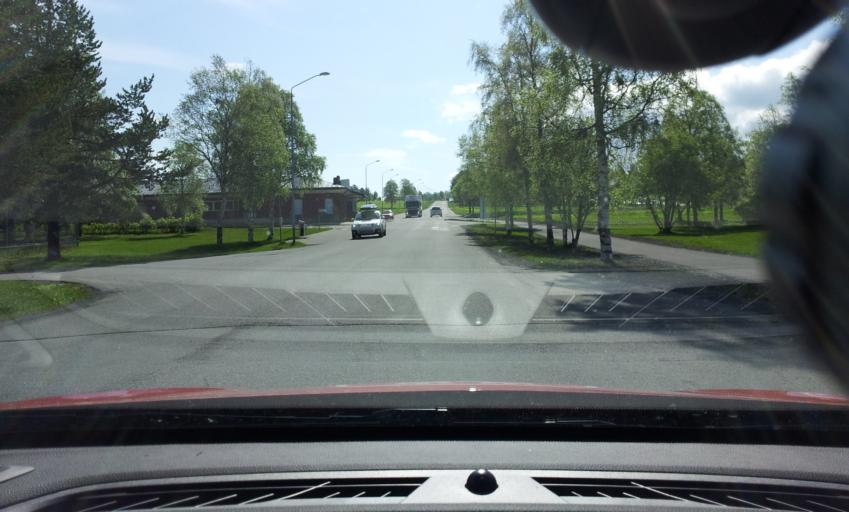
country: SE
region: Jaemtland
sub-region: Krokoms Kommun
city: Krokom
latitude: 63.1909
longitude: 14.4933
